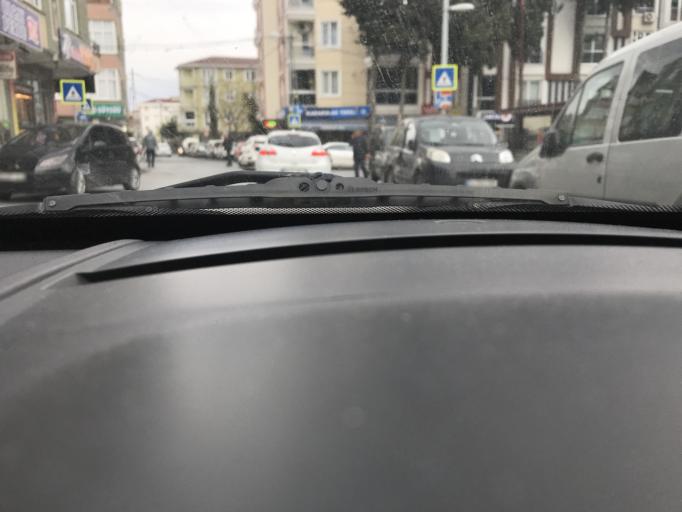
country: TR
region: Istanbul
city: Yakuplu
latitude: 41.0033
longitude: 28.6941
